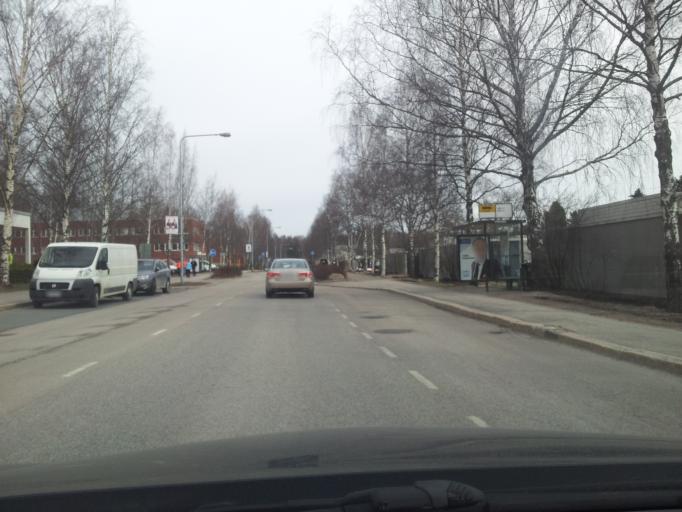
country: FI
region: Uusimaa
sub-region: Helsinki
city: Otaniemi
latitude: 60.1834
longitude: 24.7949
